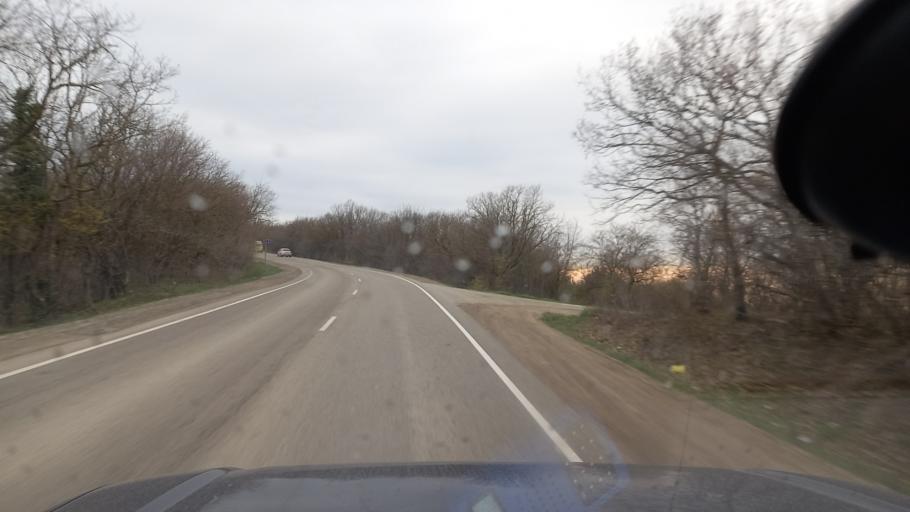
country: RU
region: Krasnodarskiy
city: Sukko
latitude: 44.8410
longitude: 37.4119
